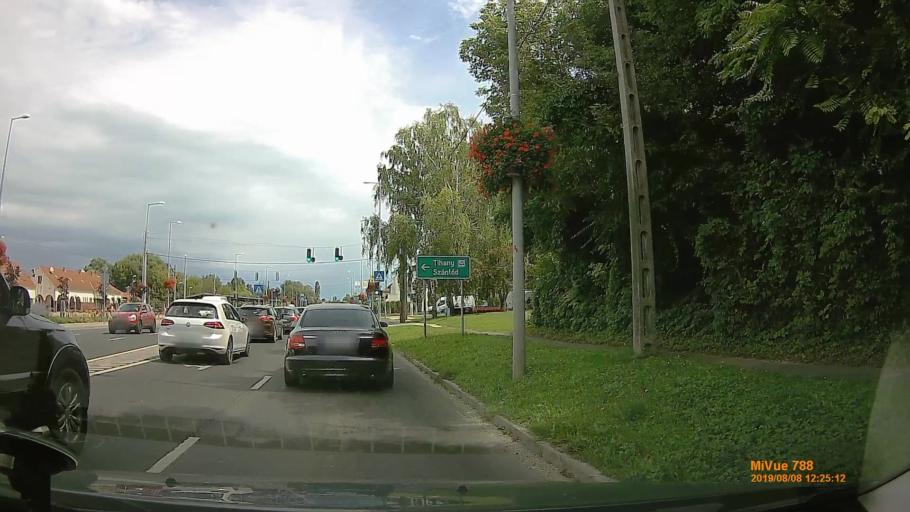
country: HU
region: Somogy
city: Zamardi
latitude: 46.8791
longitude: 17.9439
